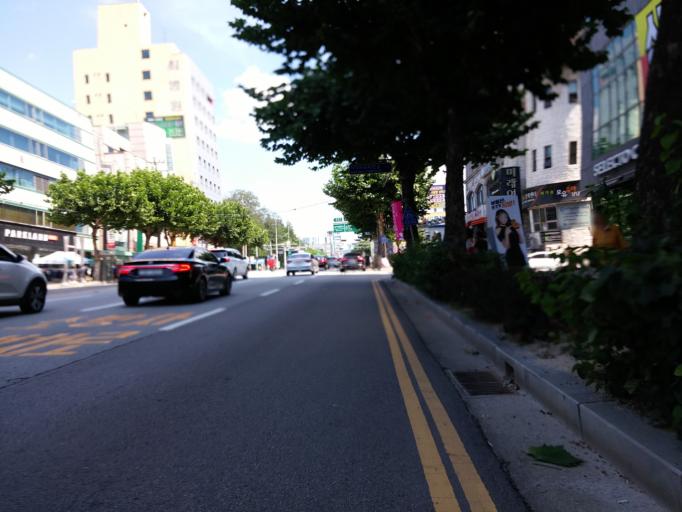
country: KR
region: Chungcheongbuk-do
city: Cheongju-si
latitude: 36.6343
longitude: 127.4516
